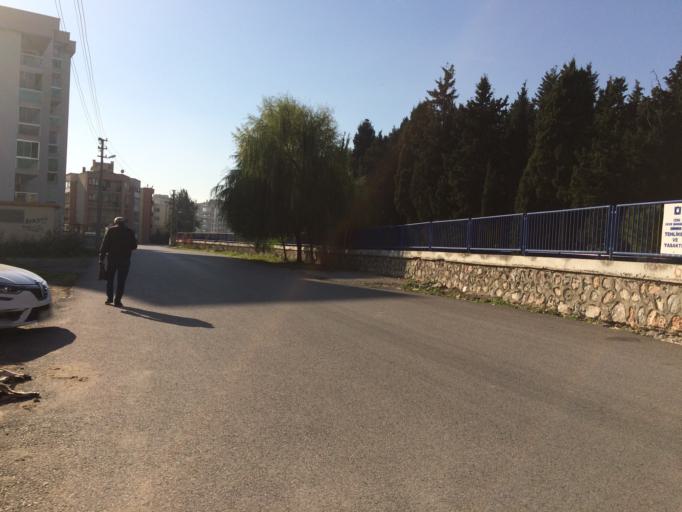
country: TR
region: Izmir
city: Karsiyaka
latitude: 38.4892
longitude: 27.0575
